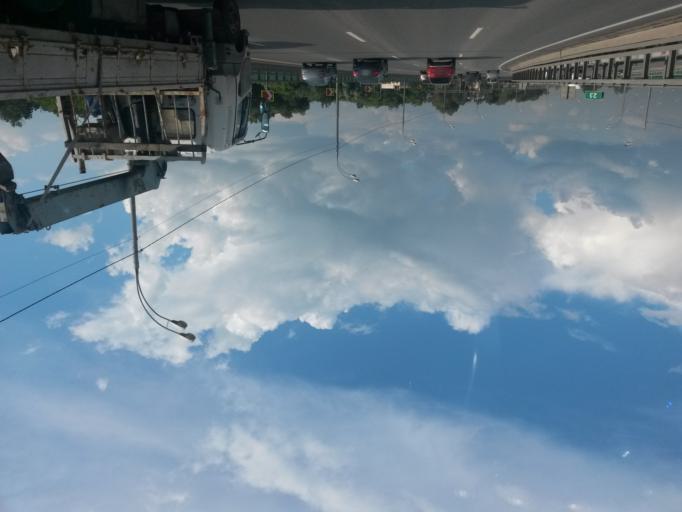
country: RU
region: Moskovskaya
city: Vidnoye
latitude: 55.5516
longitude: 37.6829
